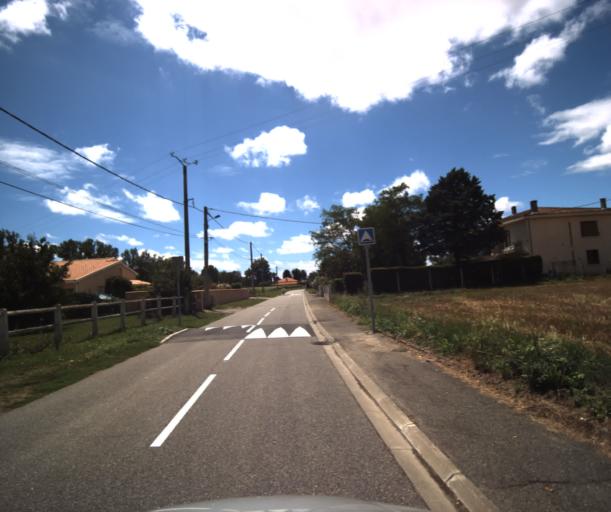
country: FR
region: Midi-Pyrenees
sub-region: Departement de la Haute-Garonne
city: Lacroix-Falgarde
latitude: 43.4888
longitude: 1.4070
